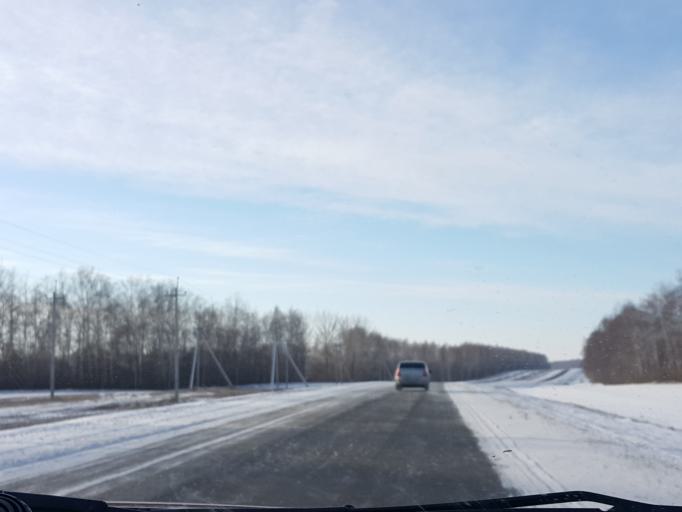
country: RU
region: Tambov
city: Znamenka
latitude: 52.3833
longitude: 41.3325
